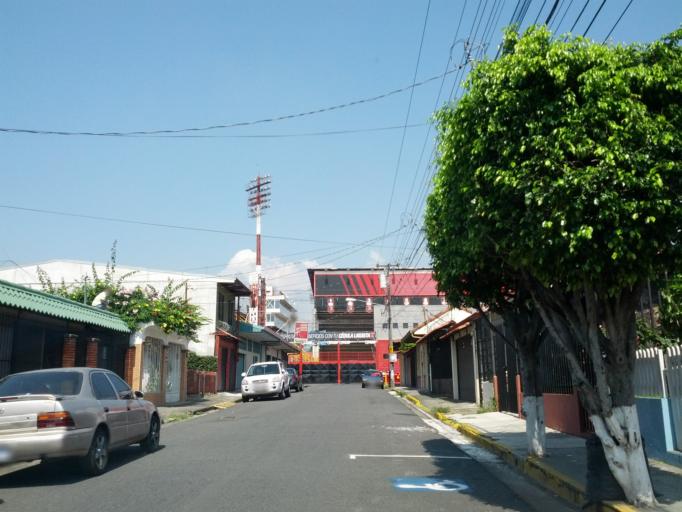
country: CR
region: Alajuela
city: Alajuela
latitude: 10.0203
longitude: -84.2091
